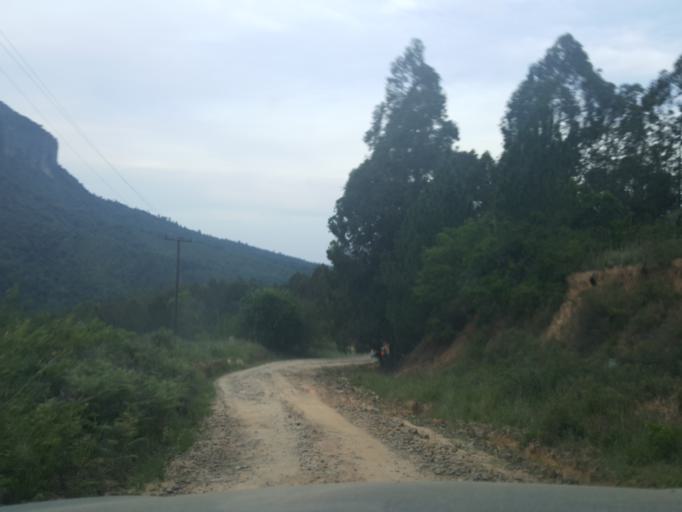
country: ZA
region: Limpopo
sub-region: Mopani District Municipality
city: Hoedspruit
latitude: -24.5953
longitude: 30.8764
